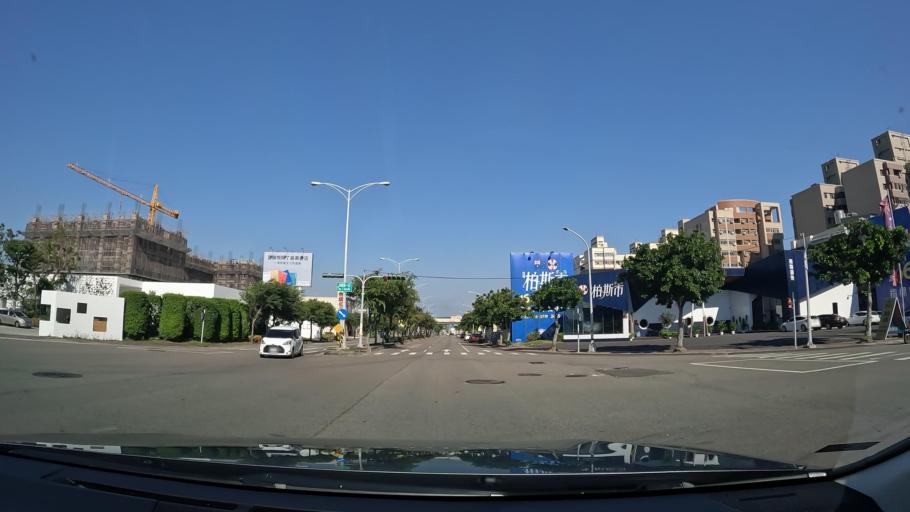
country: TW
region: Taiwan
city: Fengyuan
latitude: 24.2625
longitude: 120.5371
